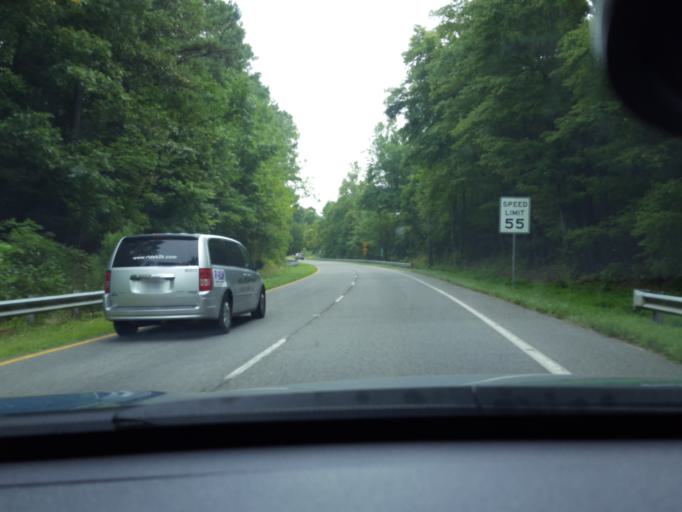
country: US
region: Virginia
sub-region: Caroline County
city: Bowling Green
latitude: 38.0554
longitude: -77.3432
